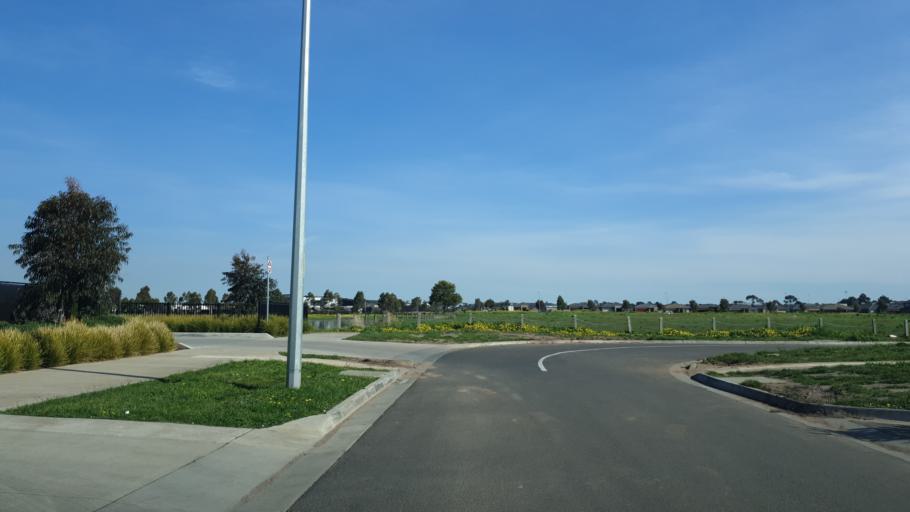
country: AU
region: Victoria
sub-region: Casey
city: Cranbourne East
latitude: -38.1088
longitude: 145.3197
